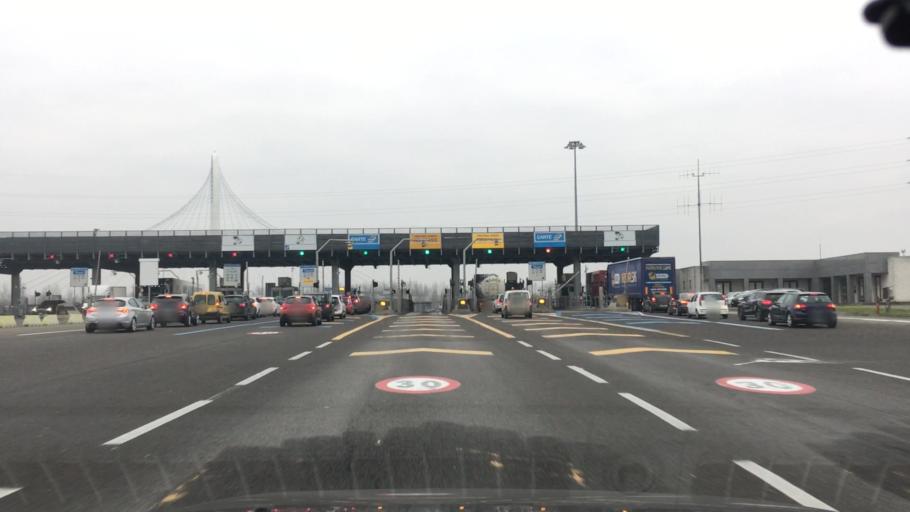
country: IT
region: Emilia-Romagna
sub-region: Provincia di Reggio Emilia
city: Reggio nell'Emilia
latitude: 44.7265
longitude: 10.6306
